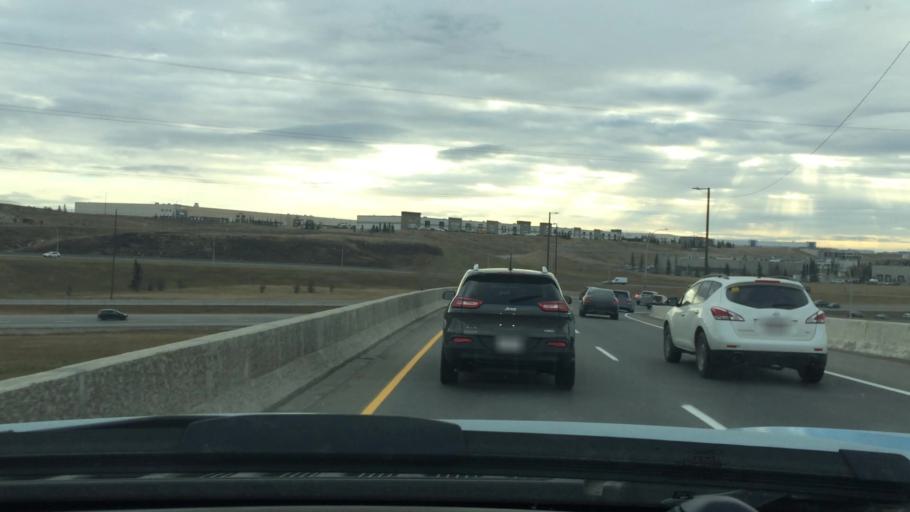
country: CA
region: Alberta
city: Calgary
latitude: 51.1254
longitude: -114.0482
